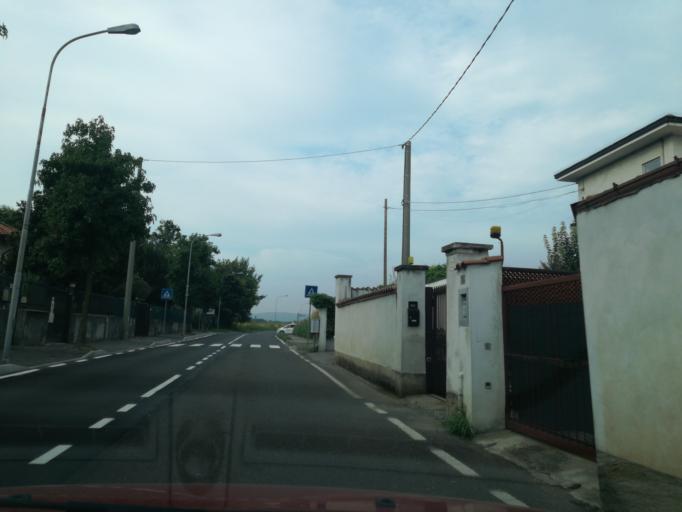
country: IT
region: Lombardy
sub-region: Provincia di Monza e Brianza
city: Vimercate
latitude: 45.6284
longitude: 9.3688
